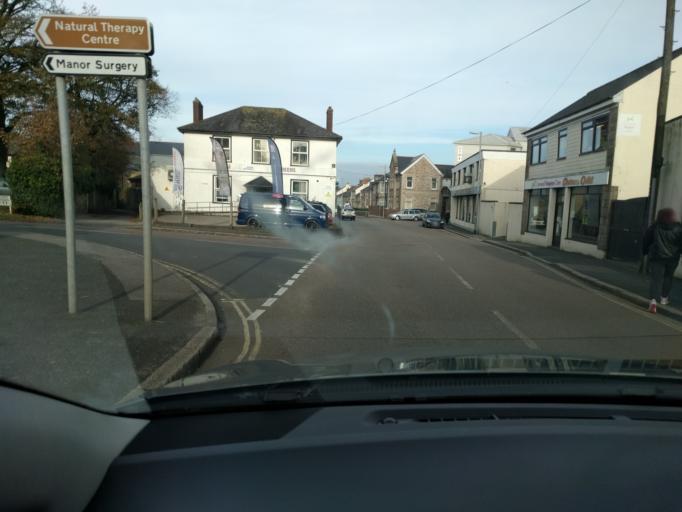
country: GB
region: England
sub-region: Cornwall
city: Redruth
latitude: 50.2339
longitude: -5.2307
